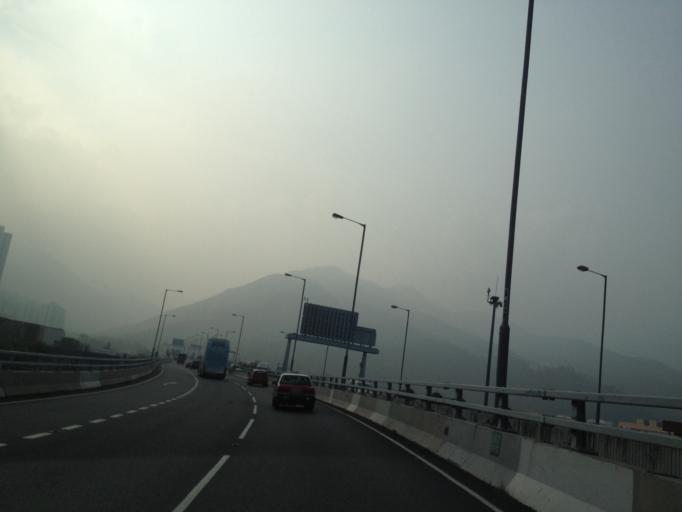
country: HK
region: Sha Tin
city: Sha Tin
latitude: 22.4102
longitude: 114.2131
